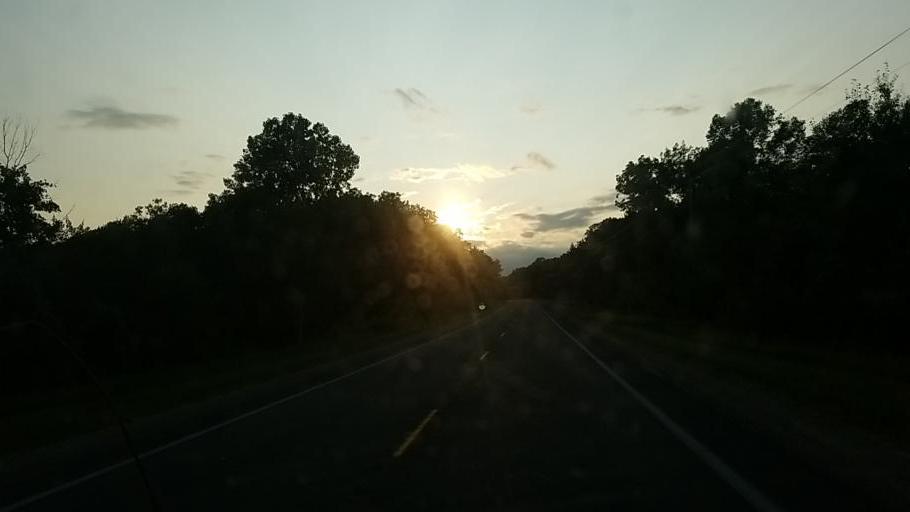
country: US
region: Michigan
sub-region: Newaygo County
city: Newaygo
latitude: 43.4037
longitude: -85.6719
